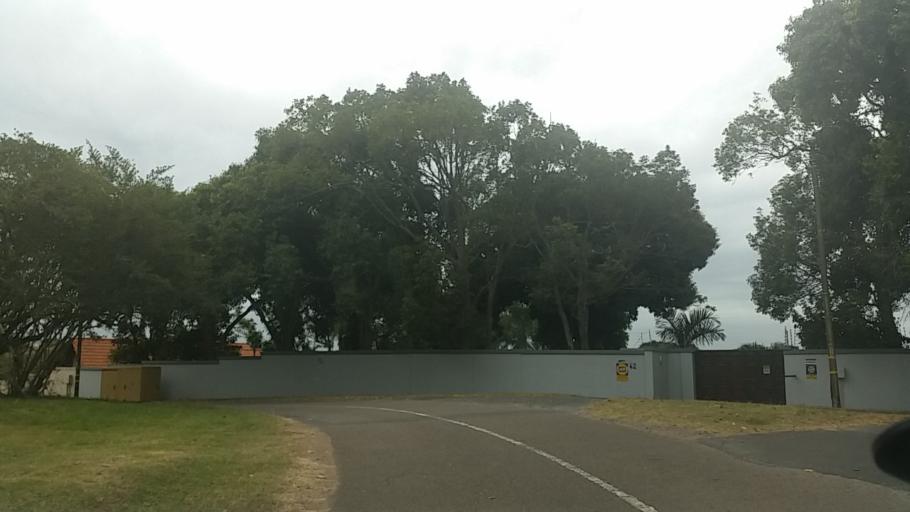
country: ZA
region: KwaZulu-Natal
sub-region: eThekwini Metropolitan Municipality
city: Berea
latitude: -29.8430
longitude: 30.9310
